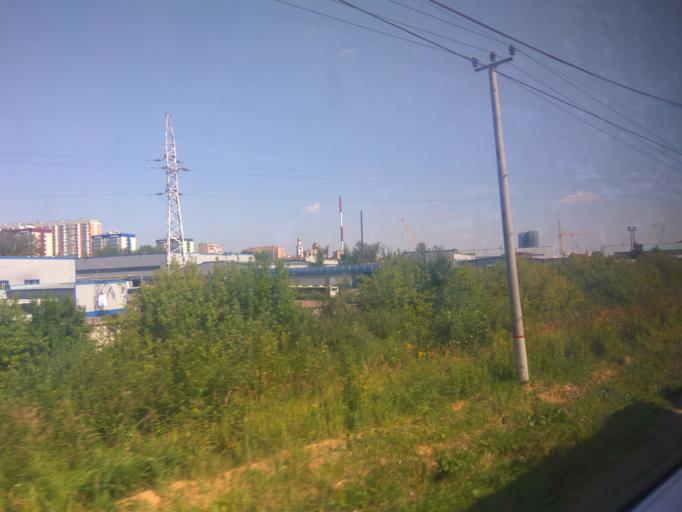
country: RU
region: Moskovskaya
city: Odintsovo
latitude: 55.6680
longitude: 37.2653
